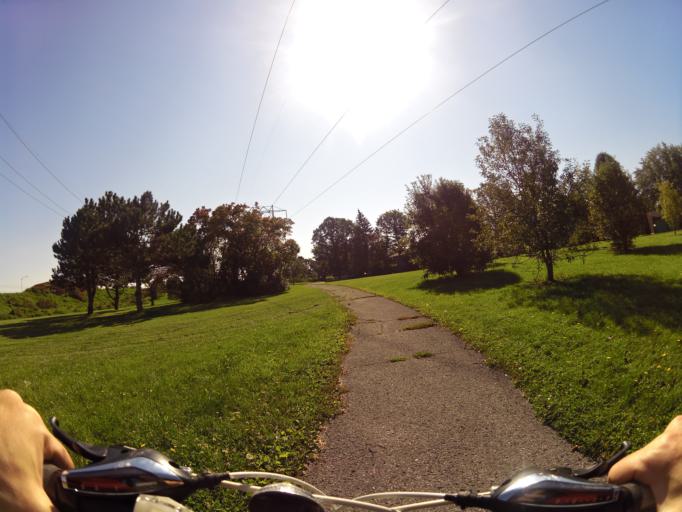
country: CA
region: Ontario
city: Bells Corners
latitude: 45.3321
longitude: -75.8953
